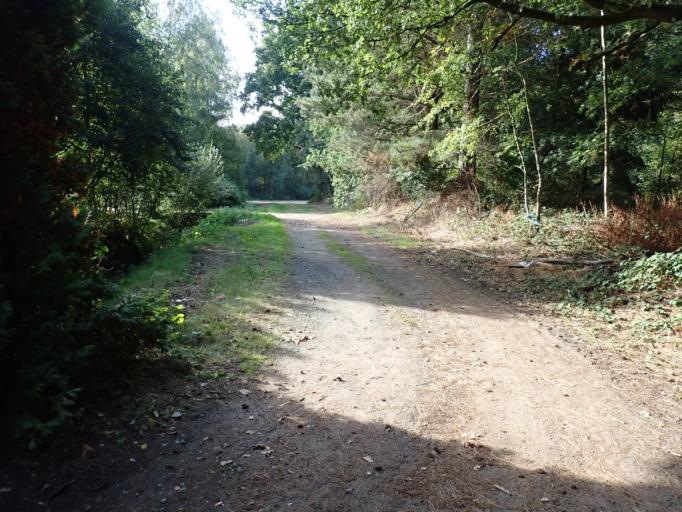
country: BE
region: Flanders
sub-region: Provincie Oost-Vlaanderen
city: Stekene
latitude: 51.2387
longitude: 4.0594
